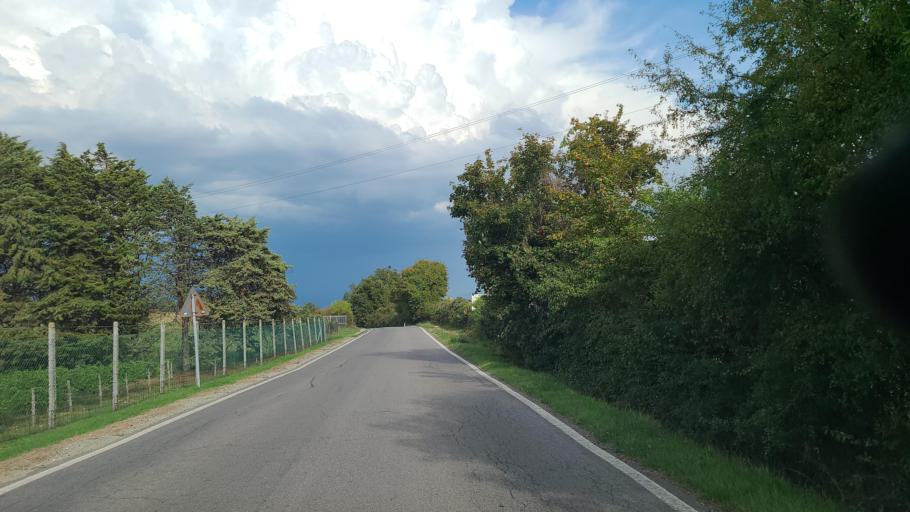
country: IT
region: Tuscany
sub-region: Province of Florence
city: Gambassi Terme
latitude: 43.4807
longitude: 10.9549
